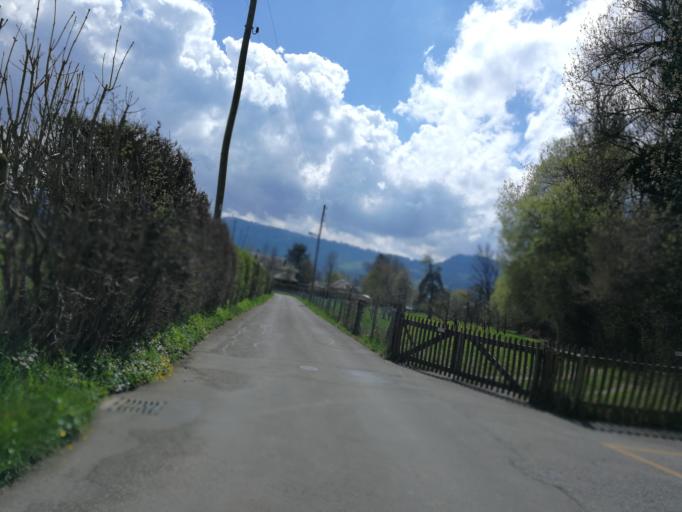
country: CH
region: Zurich
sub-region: Bezirk Meilen
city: Hombrechtikon
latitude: 47.2367
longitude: 8.7869
